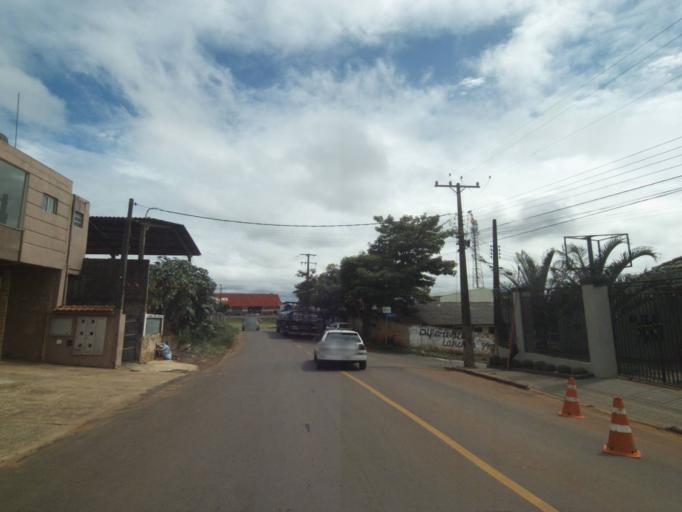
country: BR
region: Parana
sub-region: Telemaco Borba
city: Telemaco Borba
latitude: -24.3309
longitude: -50.6445
